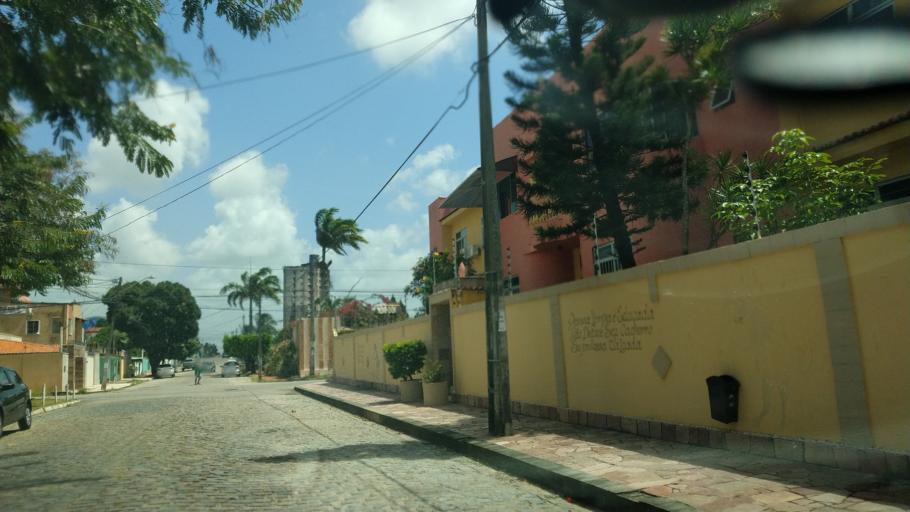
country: BR
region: Rio Grande do Norte
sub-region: Natal
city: Natal
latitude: -5.8628
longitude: -35.1956
